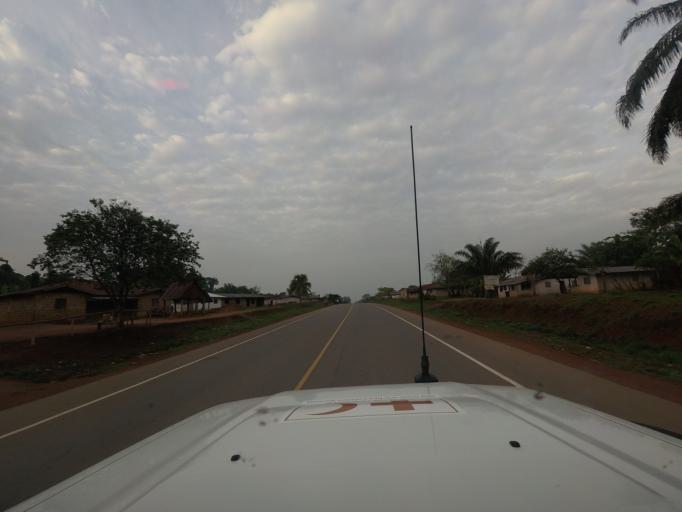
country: LR
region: Nimba
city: Sanniquellie
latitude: 7.1974
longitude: -9.0198
